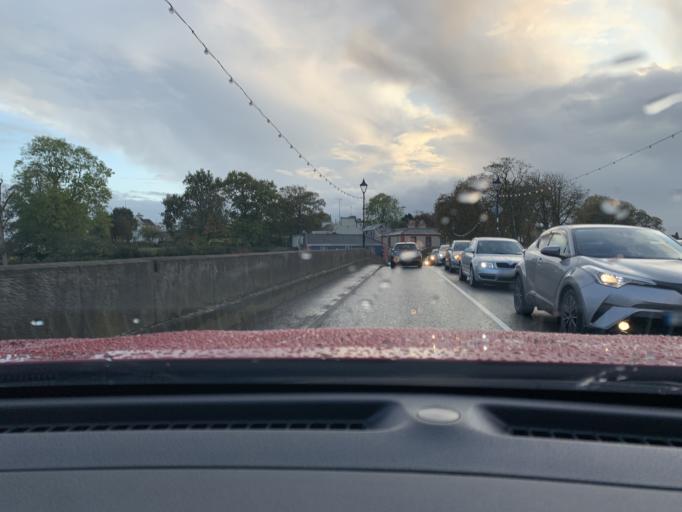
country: IE
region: Connaught
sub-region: County Leitrim
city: Carrick-on-Shannon
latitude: 53.9433
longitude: -8.0956
